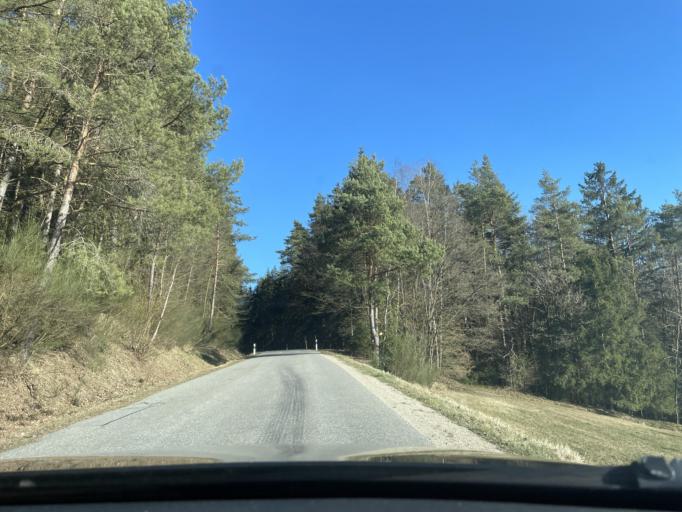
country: DE
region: Bavaria
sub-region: Lower Bavaria
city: Geiersthal
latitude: 49.0682
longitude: 12.9411
